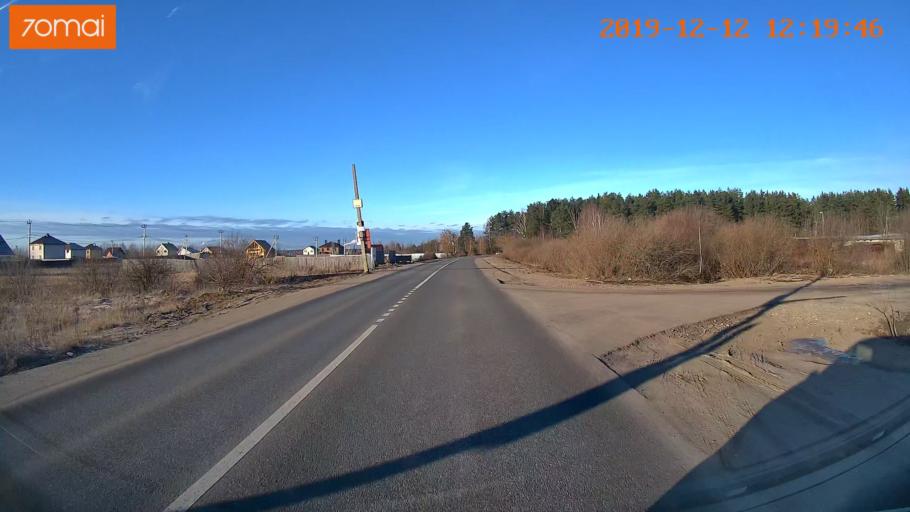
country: RU
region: Ivanovo
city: Kokhma
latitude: 56.9601
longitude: 41.0986
